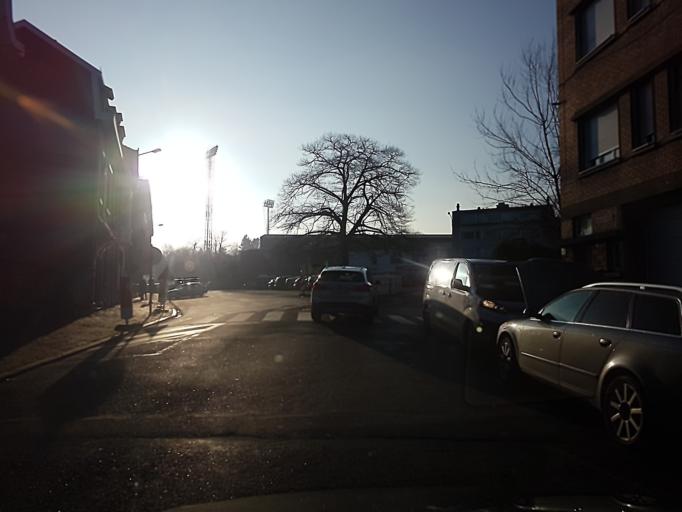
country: BE
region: Wallonia
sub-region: Province de Liege
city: Verviers
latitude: 50.5866
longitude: 5.8722
